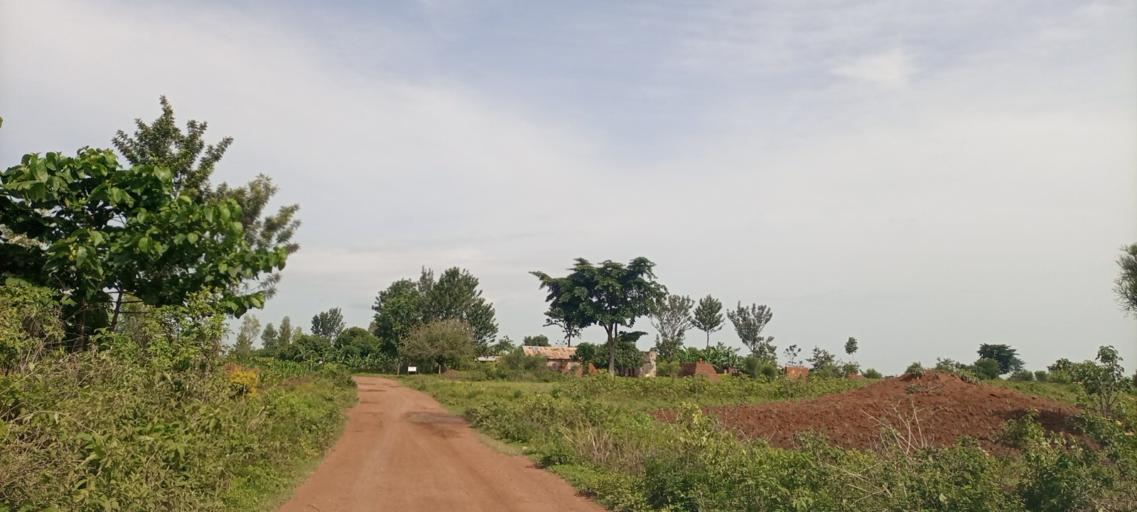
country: UG
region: Eastern Region
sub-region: Mbale District
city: Mbale
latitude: 1.1296
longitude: 34.0431
